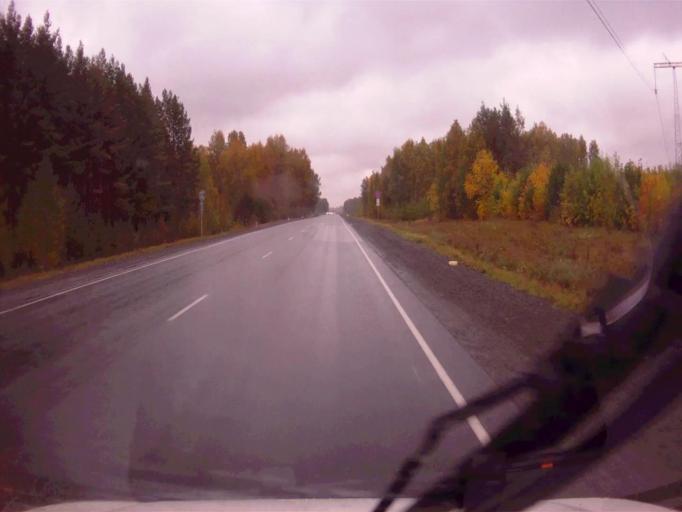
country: RU
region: Chelyabinsk
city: Roshchino
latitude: 55.3822
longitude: 61.1385
